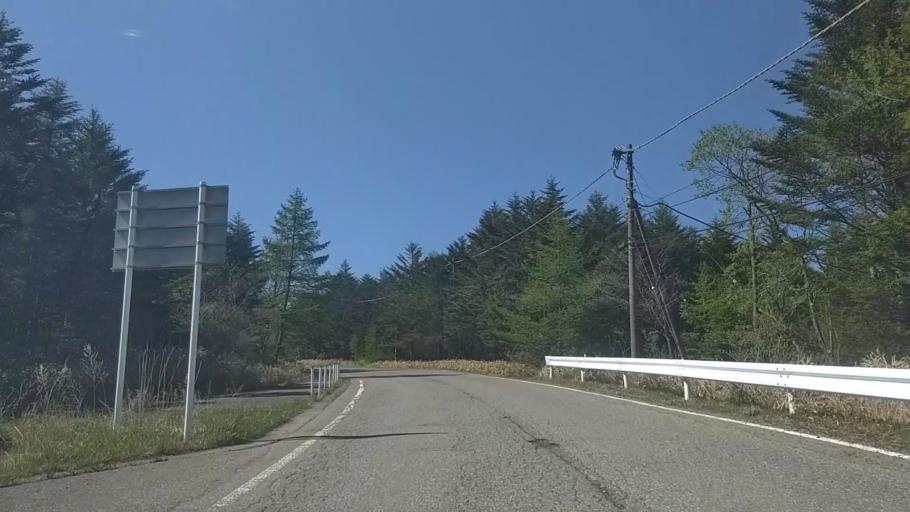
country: JP
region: Yamanashi
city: Nirasaki
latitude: 35.9451
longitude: 138.4196
